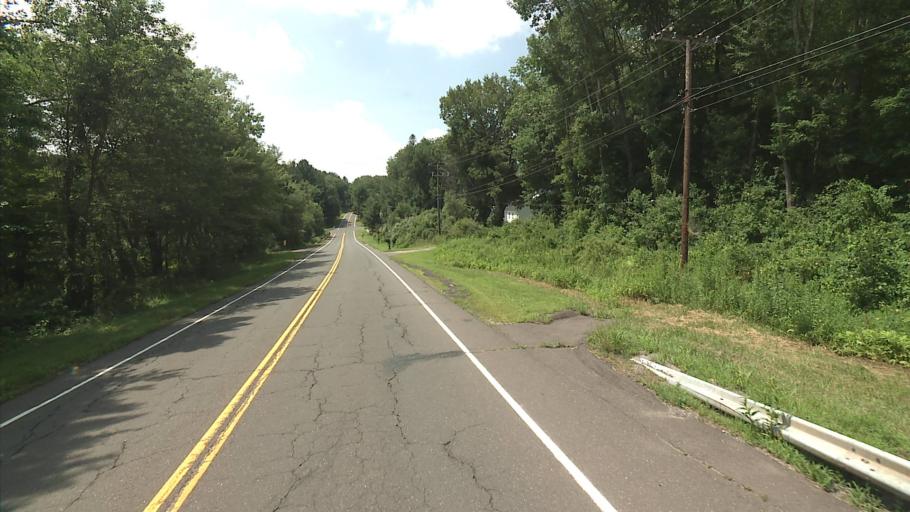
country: US
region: Connecticut
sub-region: Tolland County
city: Coventry Lake
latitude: 41.7917
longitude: -72.3531
